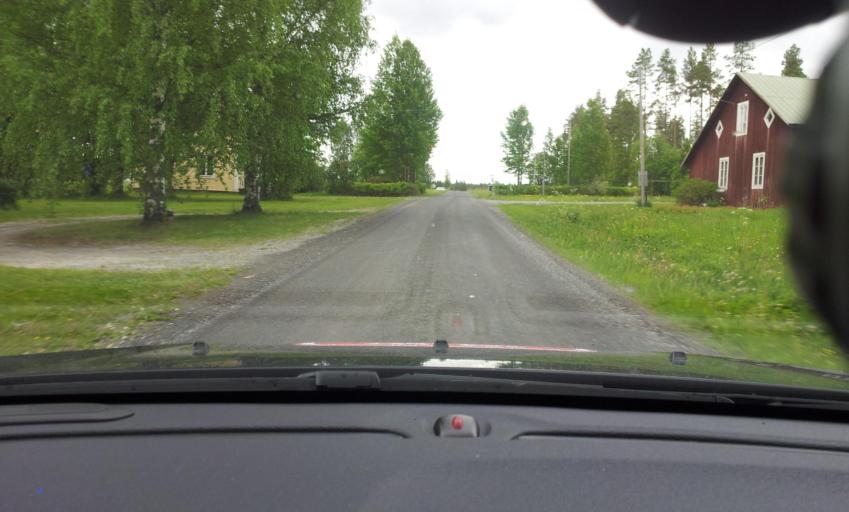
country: SE
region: Jaemtland
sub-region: OEstersunds Kommun
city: Brunflo
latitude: 63.1577
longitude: 15.0144
